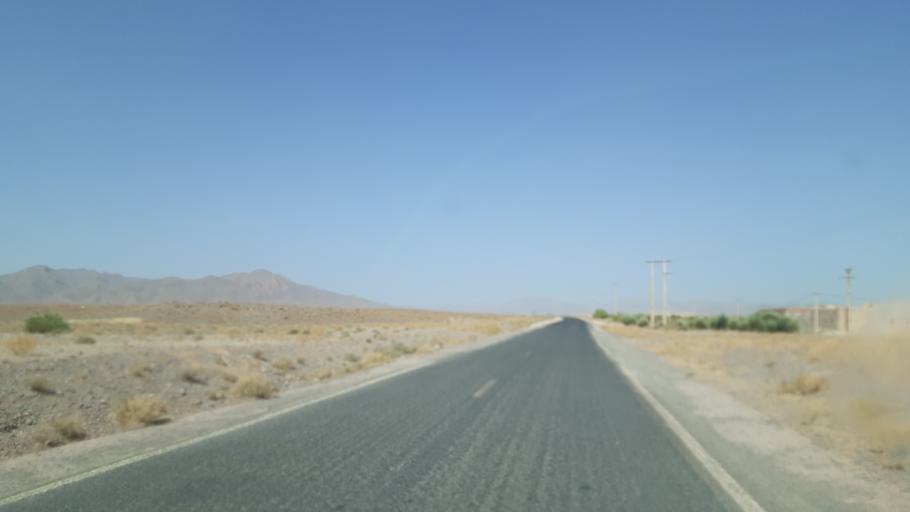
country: MA
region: Meknes-Tafilalet
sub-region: Errachidia
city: Amouguer
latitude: 32.2366
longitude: -4.6243
